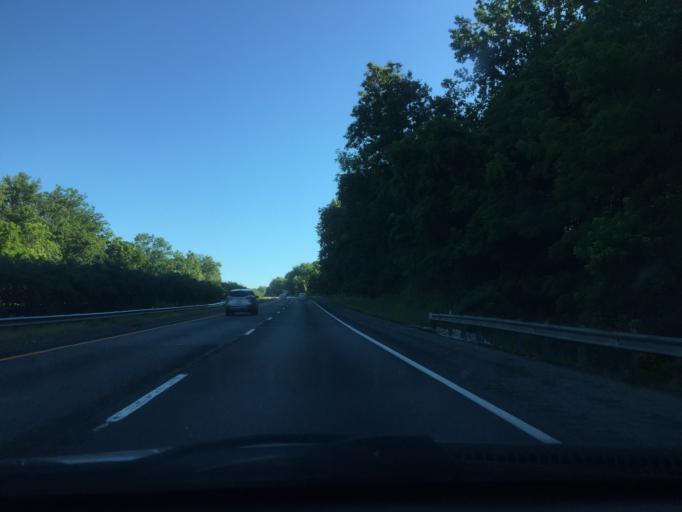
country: US
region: Maryland
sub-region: Baltimore County
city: Hunt Valley
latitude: 39.5143
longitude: -76.6626
